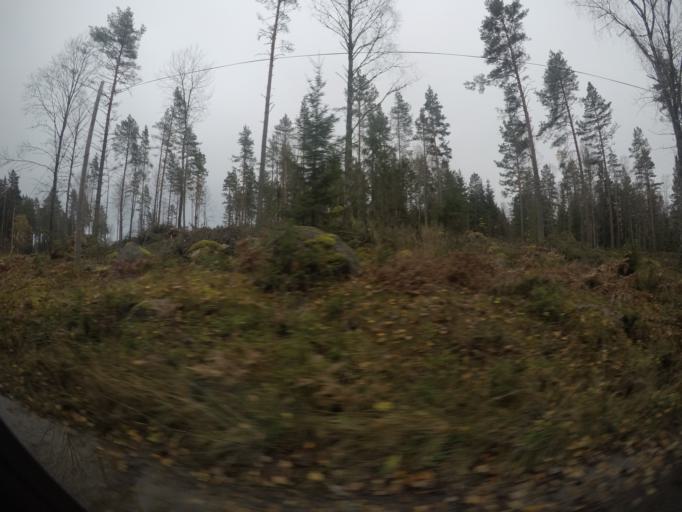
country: SE
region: Vaestmanland
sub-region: Surahammars Kommun
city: Ramnas
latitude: 59.7430
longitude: 16.1526
